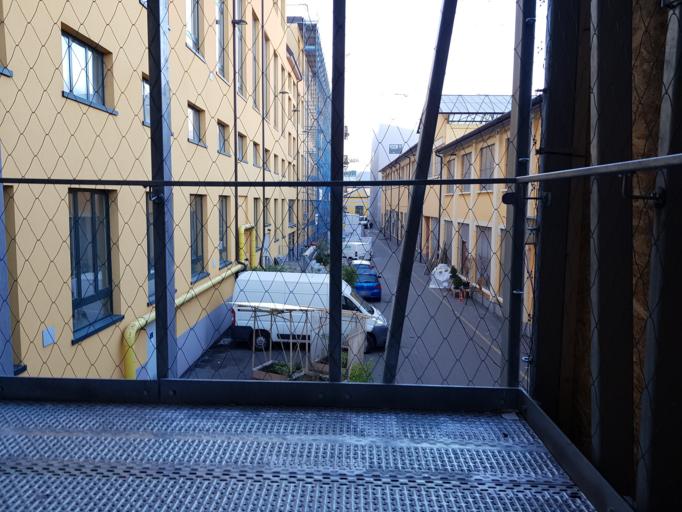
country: IT
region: Lombardy
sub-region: Citta metropolitana di Milano
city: Milano
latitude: 45.4524
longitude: 9.1637
